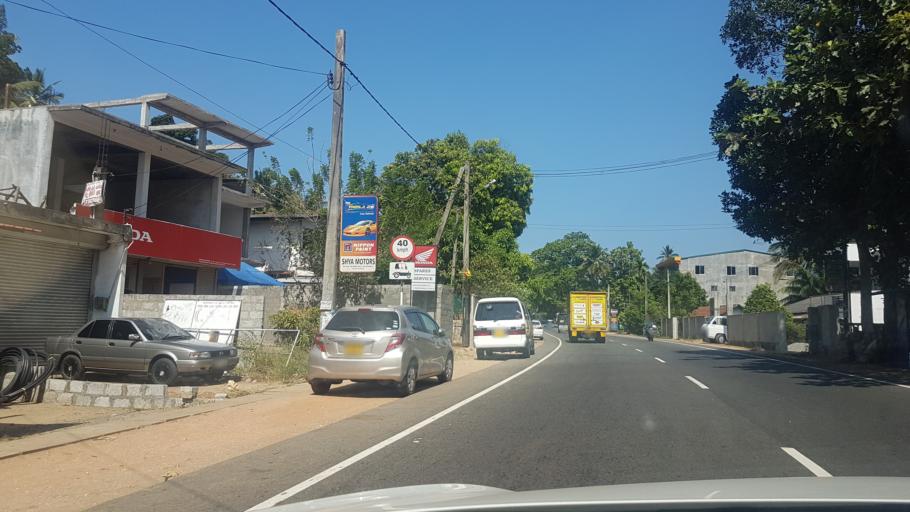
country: LK
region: North Western
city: Kurunegala
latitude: 7.3318
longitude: 80.2967
